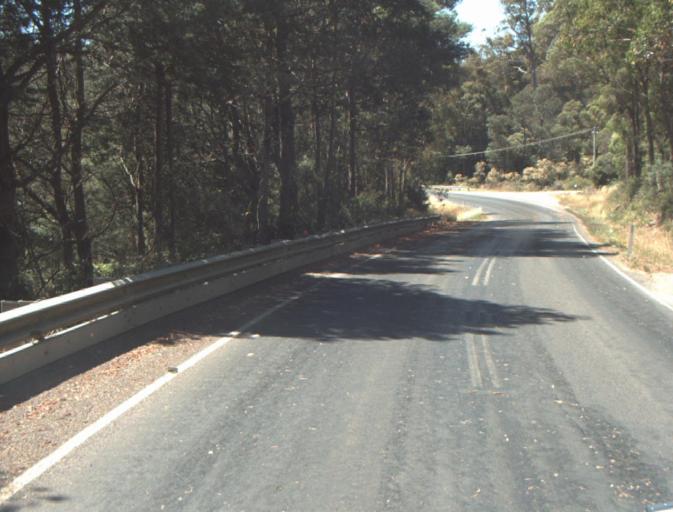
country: AU
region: Tasmania
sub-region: Launceston
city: Newstead
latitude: -41.3244
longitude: 147.3586
